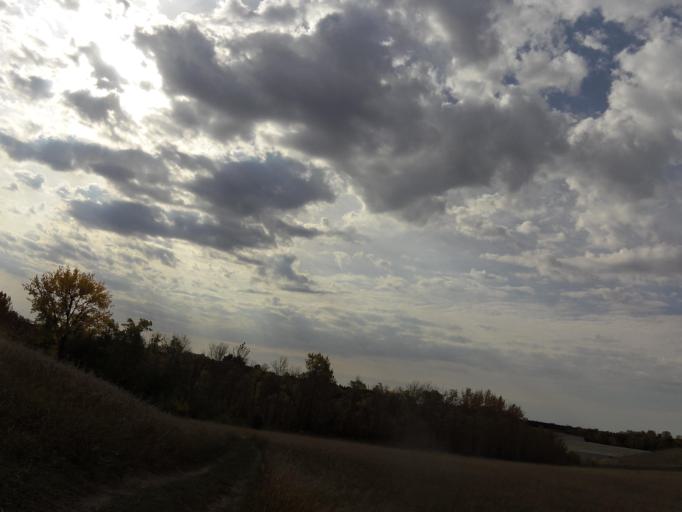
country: US
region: North Dakota
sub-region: Pembina County
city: Cavalier
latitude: 48.7803
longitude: -97.7449
